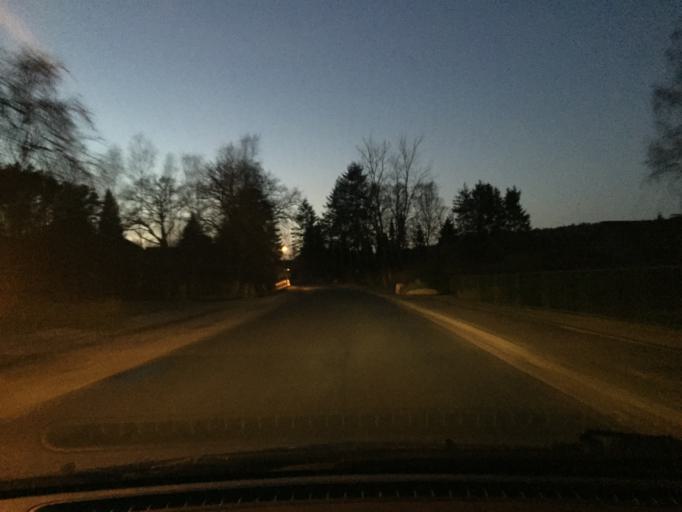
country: DE
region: Lower Saxony
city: Gohrde
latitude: 53.1653
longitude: 10.8640
